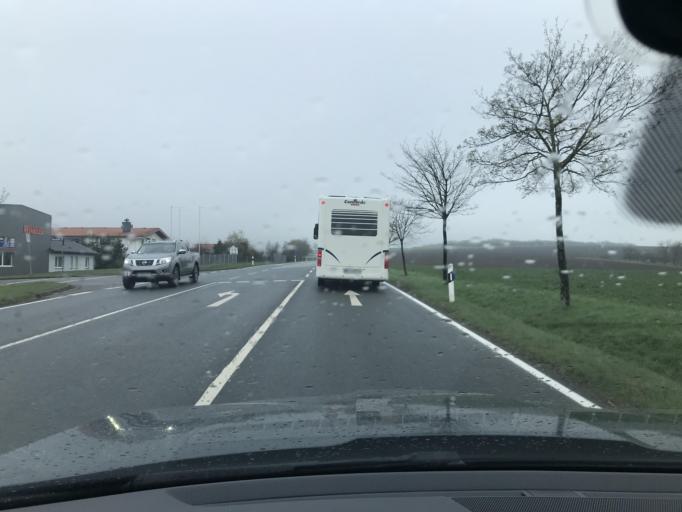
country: DE
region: Saxony-Anhalt
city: Harzgerode
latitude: 51.6333
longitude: 11.1465
